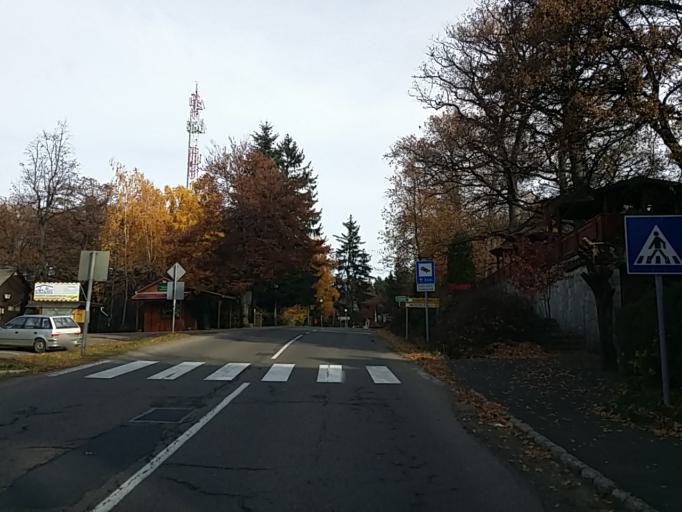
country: HU
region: Heves
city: Paradsasvar
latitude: 47.8687
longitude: 19.9783
